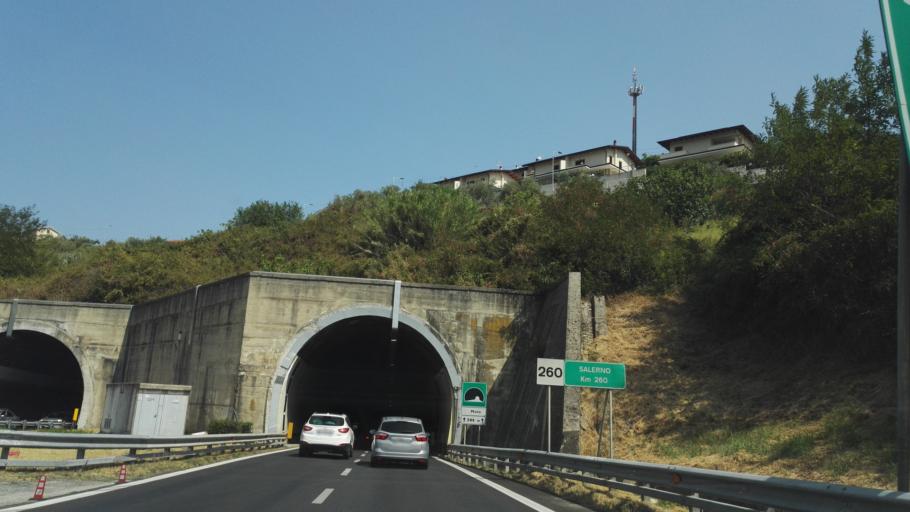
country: IT
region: Calabria
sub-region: Provincia di Cosenza
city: Rosario
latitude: 39.2917
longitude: 16.2388
